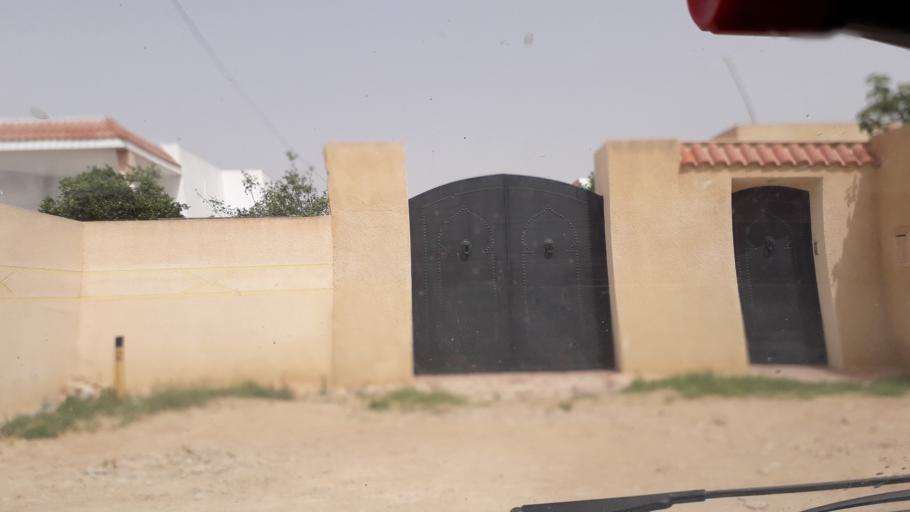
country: TN
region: Safaqis
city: Al Qarmadah
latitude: 34.8031
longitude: 10.7721
